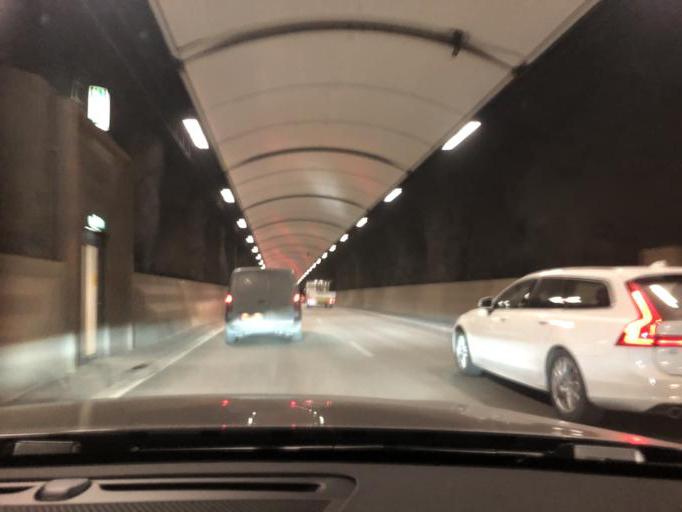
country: SE
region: Stockholm
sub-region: Stockholms Kommun
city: Arsta
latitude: 59.2916
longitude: 18.0599
